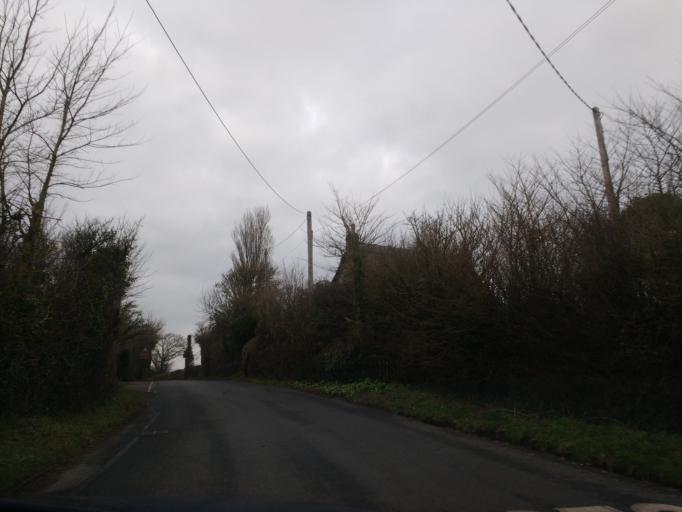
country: GB
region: England
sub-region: Isle of Wight
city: Shalfleet
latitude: 50.6877
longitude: -1.3995
